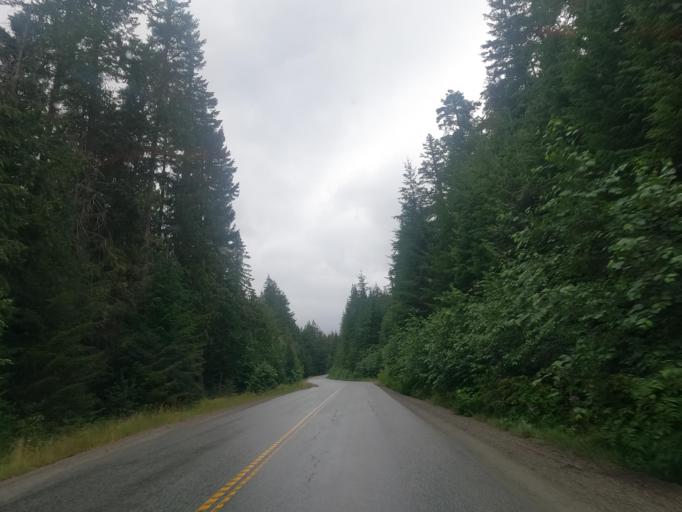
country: CA
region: British Columbia
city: Pemberton
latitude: 50.3172
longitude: -122.5640
